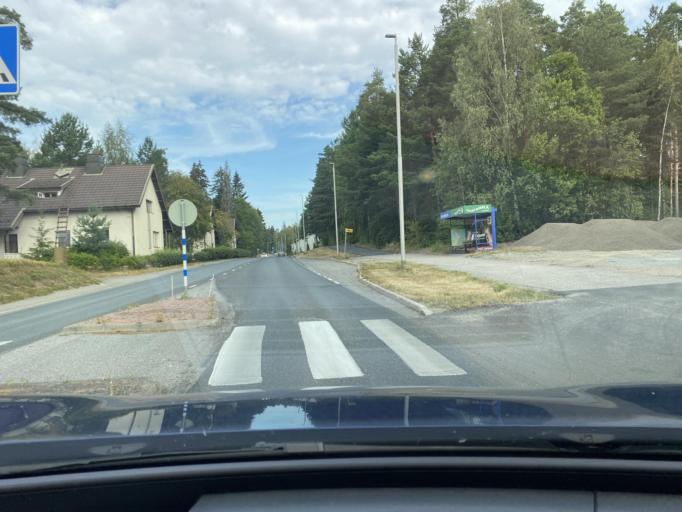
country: FI
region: Pirkanmaa
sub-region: Lounais-Pirkanmaa
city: Vammala
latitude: 61.3522
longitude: 22.8962
